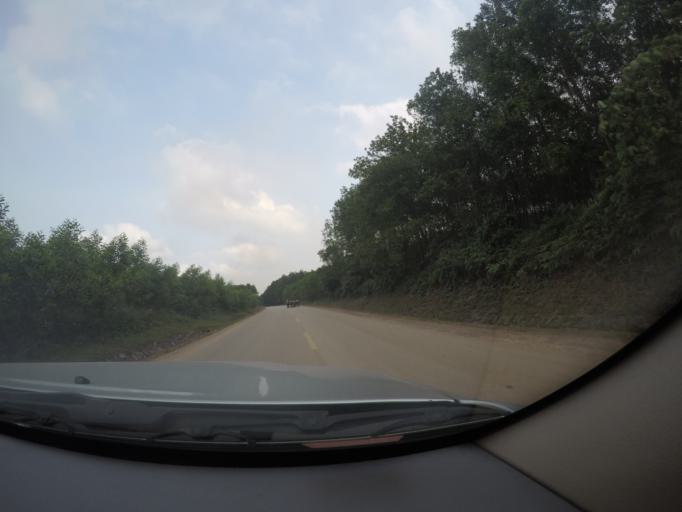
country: VN
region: Quang Binh
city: Kien Giang
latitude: 17.1174
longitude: 106.8017
